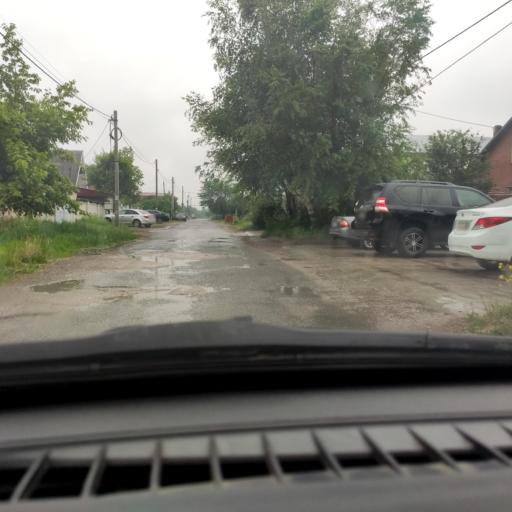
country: RU
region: Samara
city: Tol'yatti
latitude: 53.5638
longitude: 49.3812
